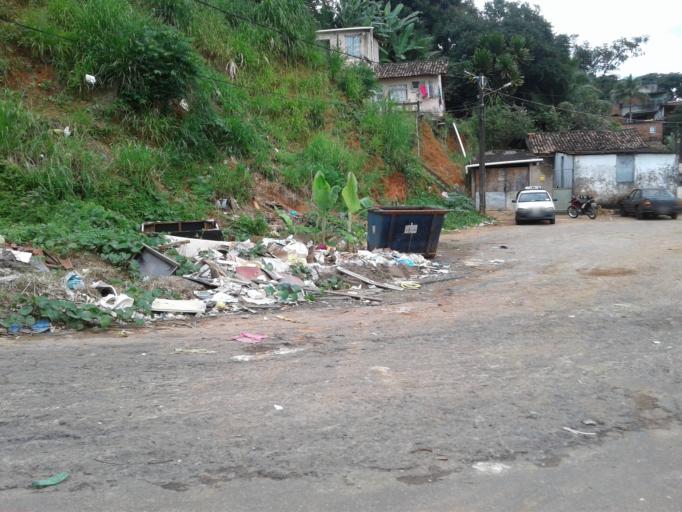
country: BR
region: Bahia
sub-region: Salvador
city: Salvador
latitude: -12.9093
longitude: -38.4734
